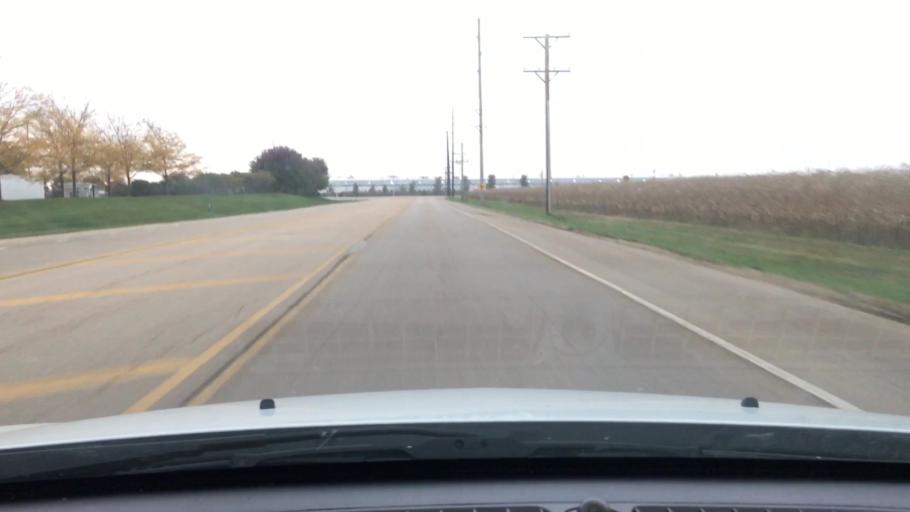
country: US
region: Illinois
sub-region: Ogle County
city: Rochelle
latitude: 41.8951
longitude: -89.0290
